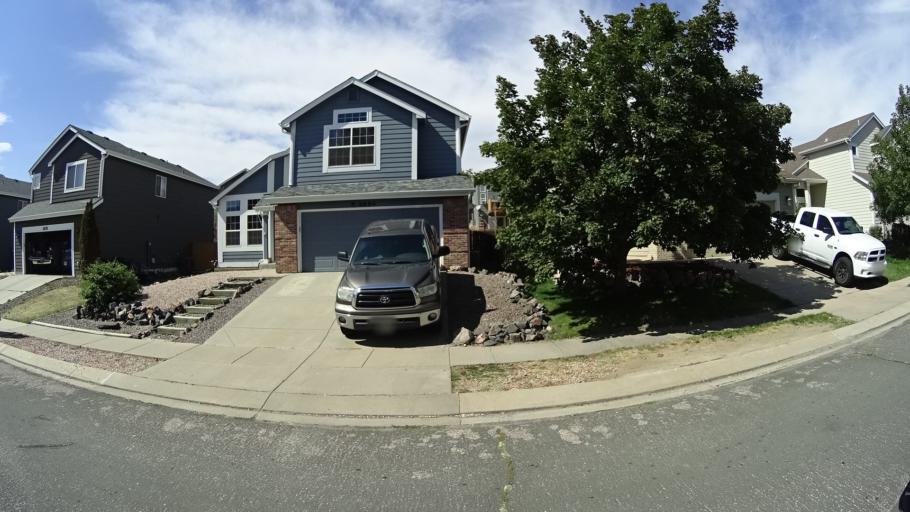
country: US
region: Colorado
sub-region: El Paso County
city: Cimarron Hills
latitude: 38.9037
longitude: -104.7155
